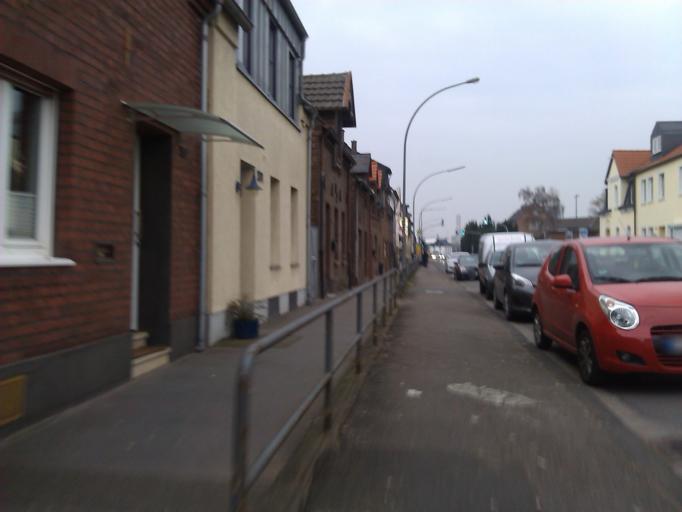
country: DE
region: North Rhine-Westphalia
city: Monheim am Rhein
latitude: 51.0689
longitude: 6.8619
